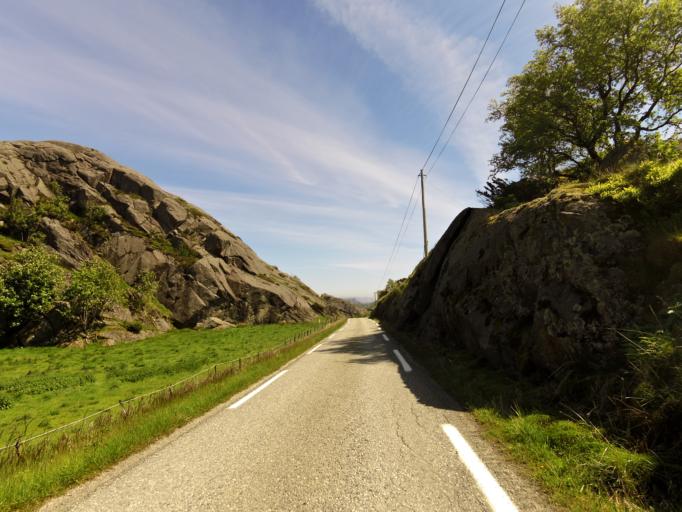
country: NO
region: Rogaland
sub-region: Sokndal
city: Hauge i Dalane
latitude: 58.3547
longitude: 6.1587
